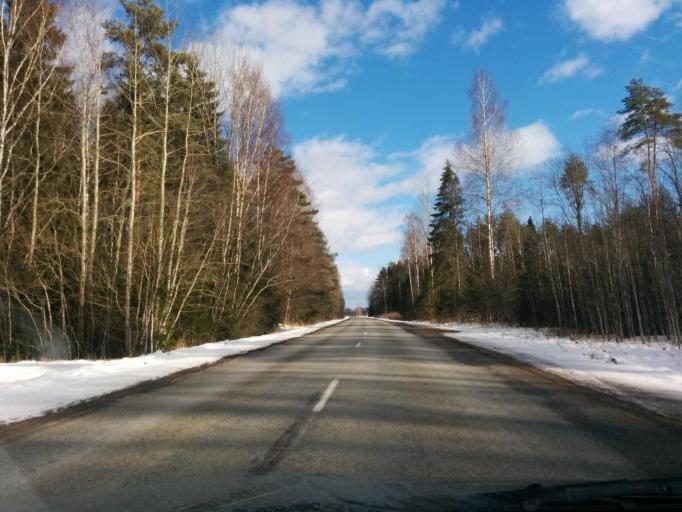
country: LV
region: Aluksnes Rajons
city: Aluksne
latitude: 57.1930
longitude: 26.9952
